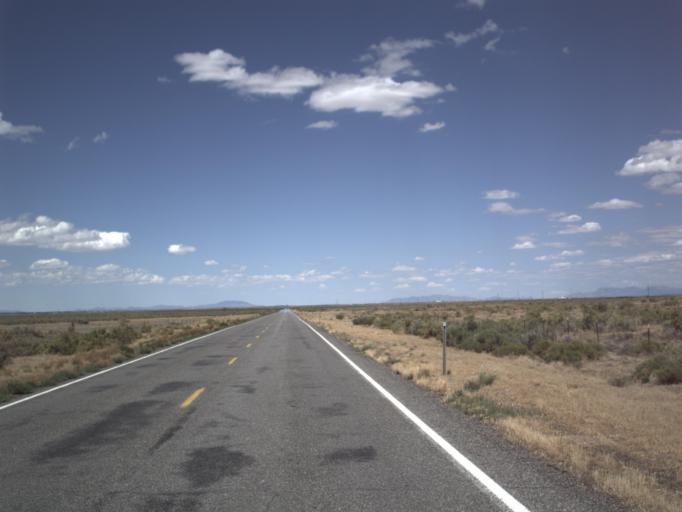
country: US
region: Utah
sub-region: Millard County
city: Delta
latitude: 39.2346
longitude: -112.4294
